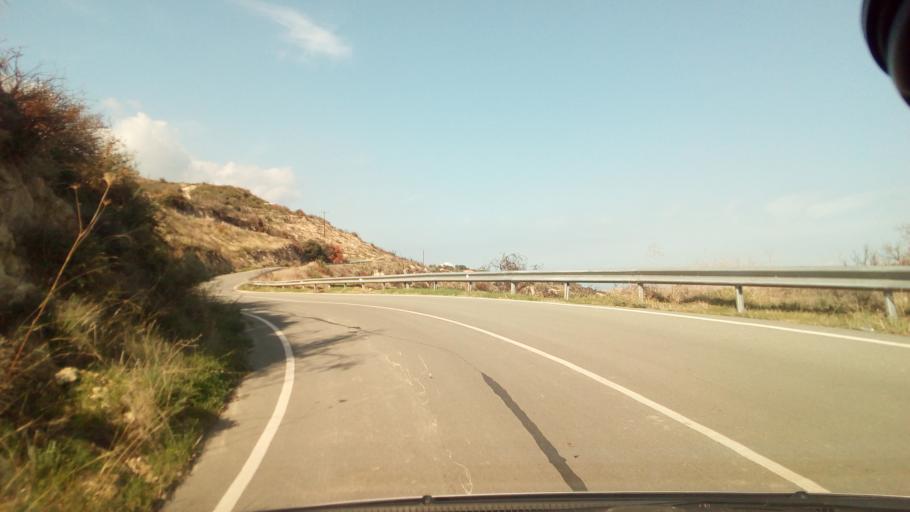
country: CY
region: Pafos
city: Polis
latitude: 34.9724
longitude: 32.4511
